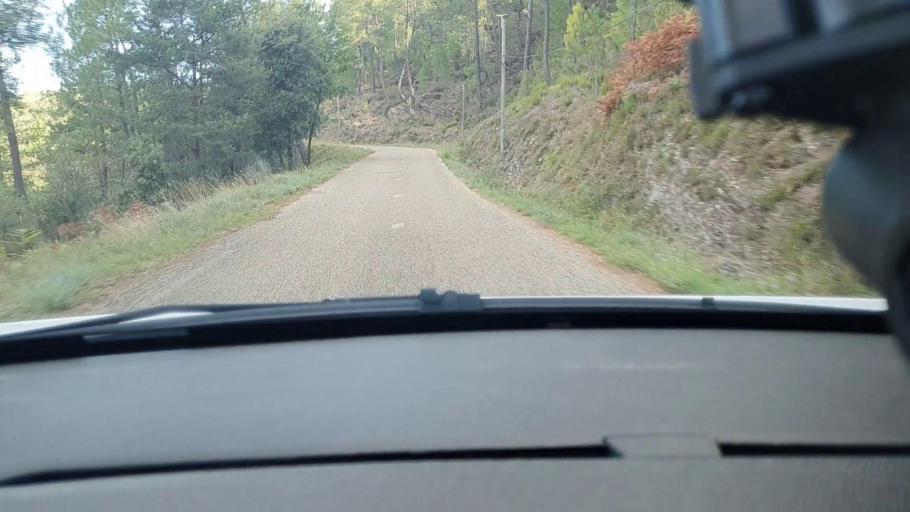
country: FR
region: Languedoc-Roussillon
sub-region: Departement du Gard
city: Besseges
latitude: 44.3294
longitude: 3.9998
